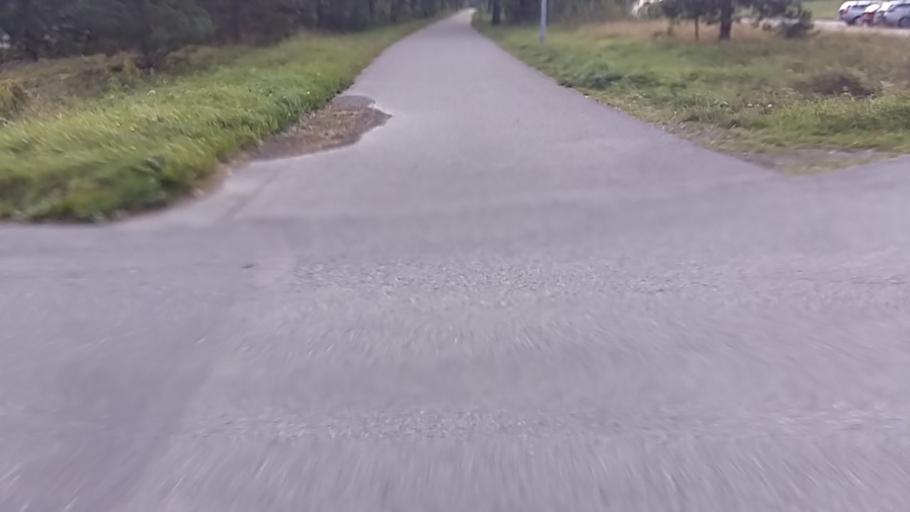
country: SE
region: Joenkoeping
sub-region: Jonkopings Kommun
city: Odensjo
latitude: 57.7453
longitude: 14.1567
